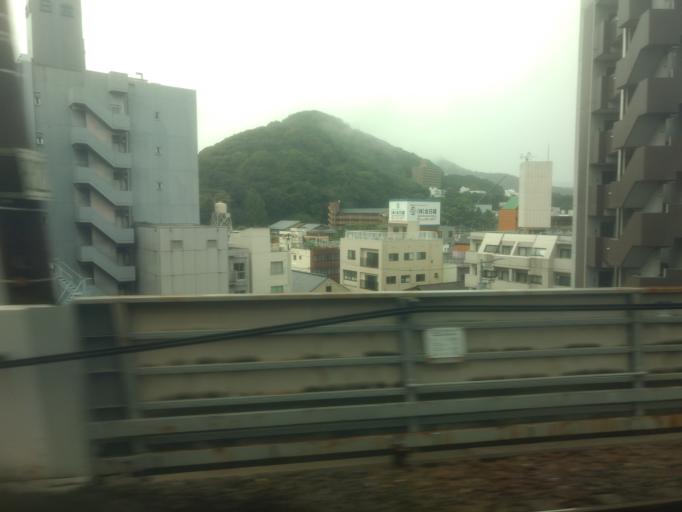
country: JP
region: Hiroshima
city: Hiroshima-shi
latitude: 34.4030
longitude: 132.4692
